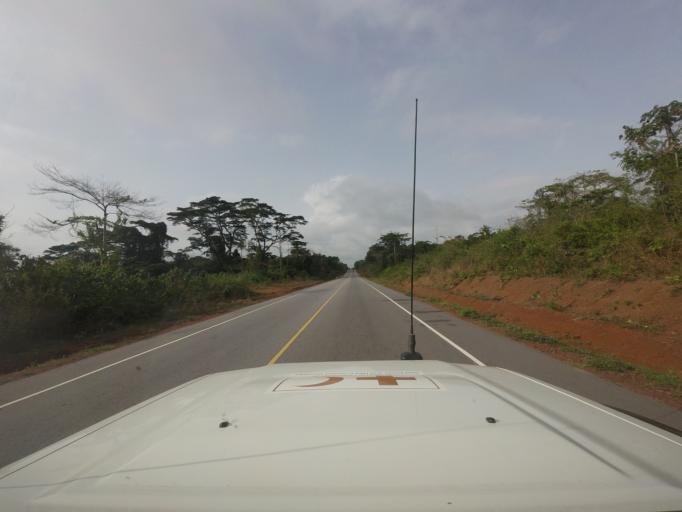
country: LR
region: Bong
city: Gbarnga
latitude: 7.0209
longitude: -9.2750
